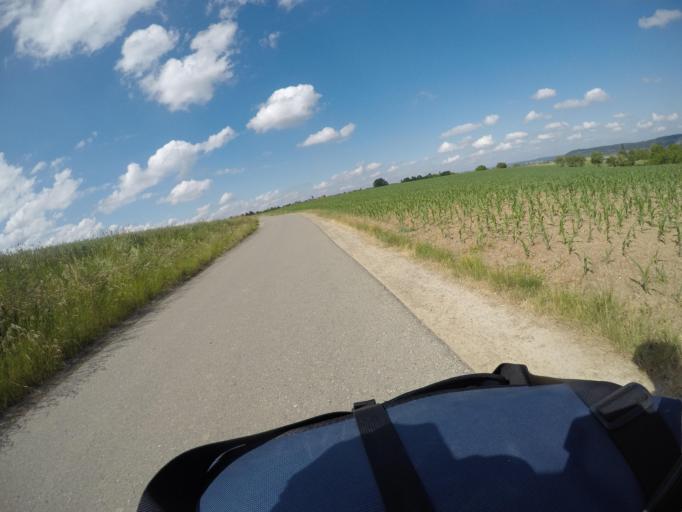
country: DE
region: Baden-Wuerttemberg
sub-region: Regierungsbezirk Stuttgart
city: Herrenberg
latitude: 48.5999
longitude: 8.8337
